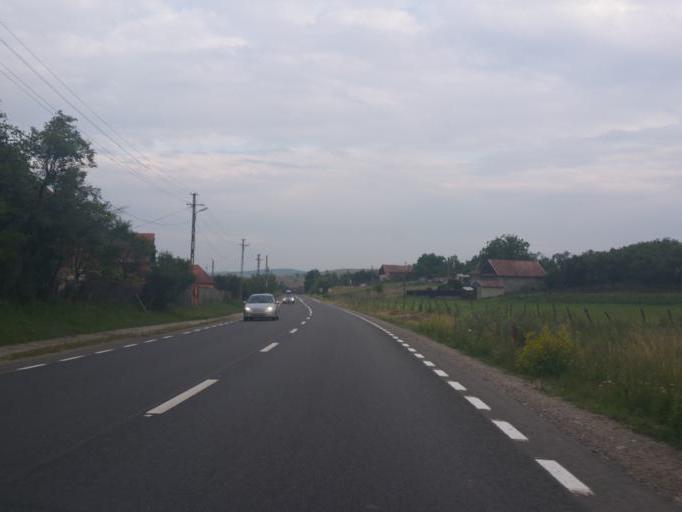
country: RO
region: Cluj
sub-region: Comuna Sanpaul
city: Sanpaul
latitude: 46.9352
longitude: 23.3923
